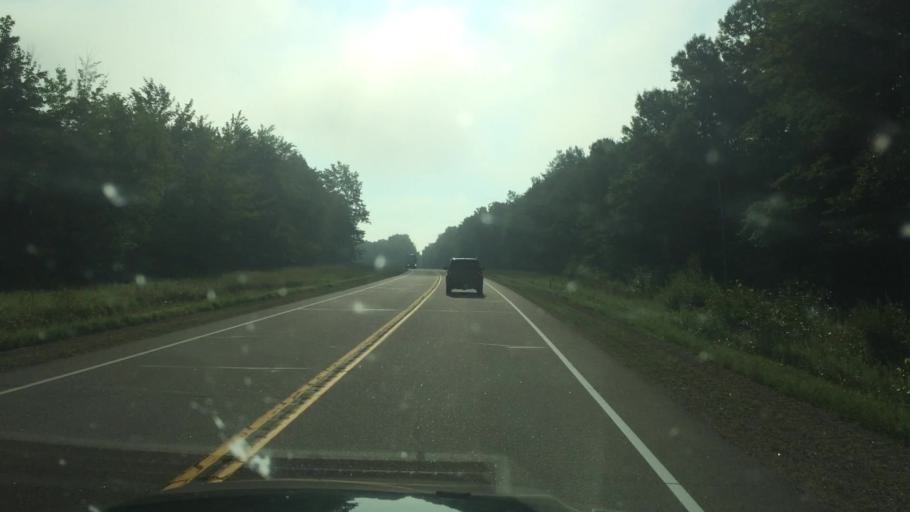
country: US
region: Wisconsin
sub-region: Langlade County
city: Antigo
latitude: 45.1440
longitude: -89.3024
